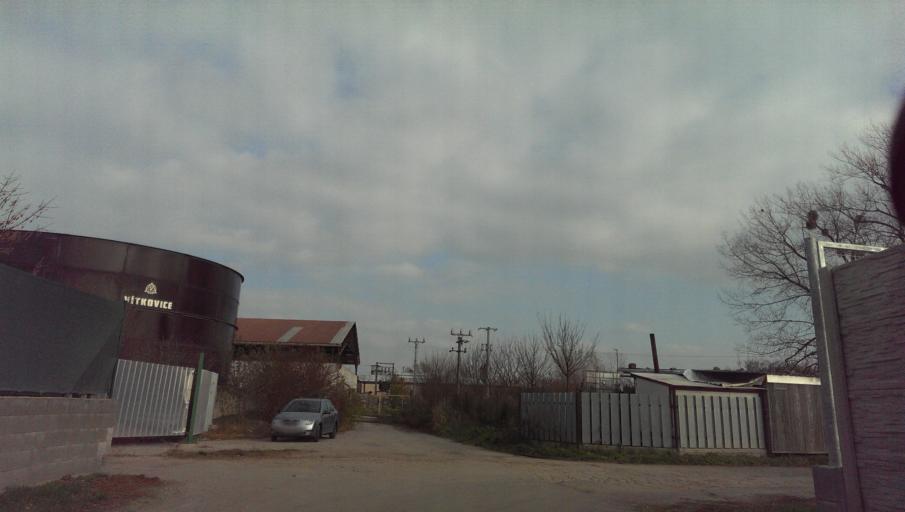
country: CZ
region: Zlin
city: Tlumacov
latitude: 49.2484
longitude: 17.5060
